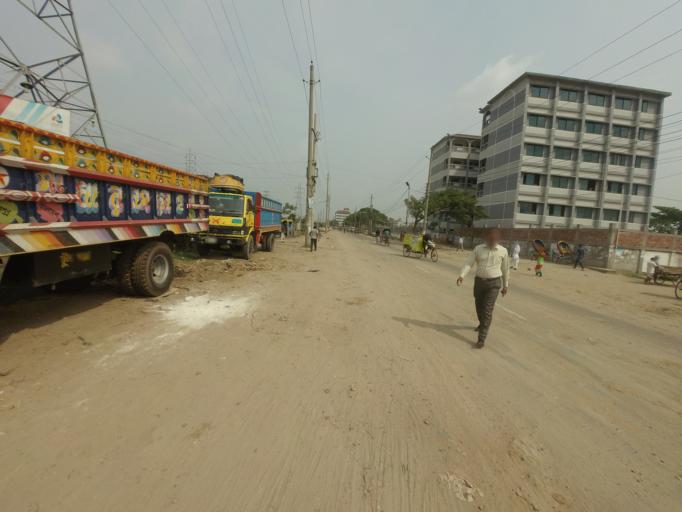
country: BD
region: Dhaka
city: Azimpur
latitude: 23.7252
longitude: 90.3696
